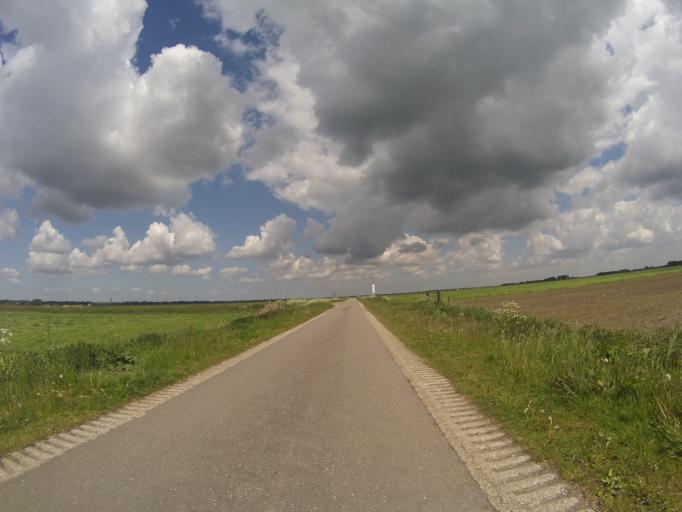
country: NL
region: Utrecht
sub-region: Gemeente Baarn
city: Baarn
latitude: 52.2355
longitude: 5.2853
